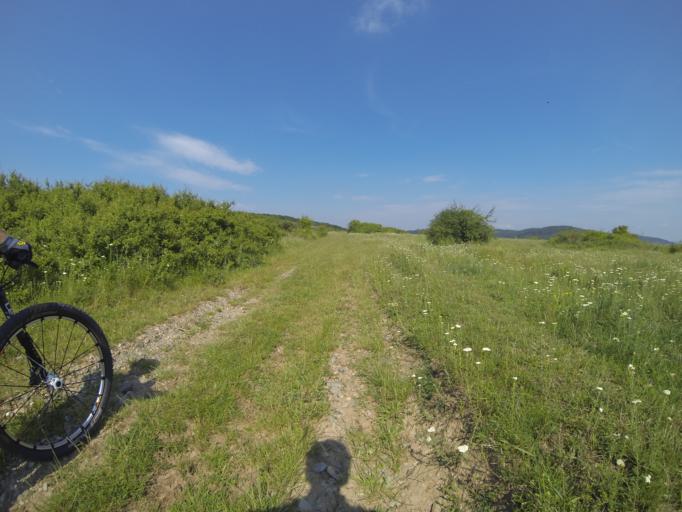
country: RO
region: Gorj
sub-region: Comuna Crusetu
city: Crusetu
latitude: 44.6122
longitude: 23.6678
